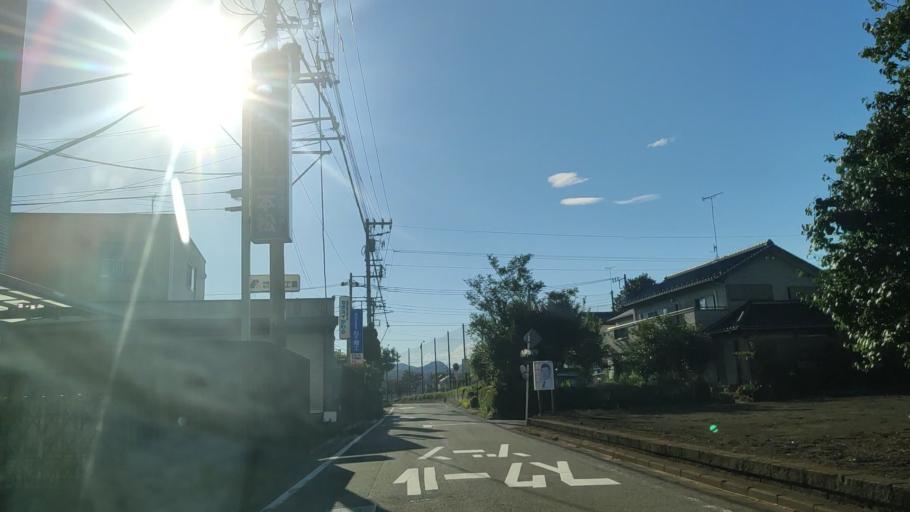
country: JP
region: Tokyo
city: Hachioji
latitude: 35.5917
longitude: 139.3155
